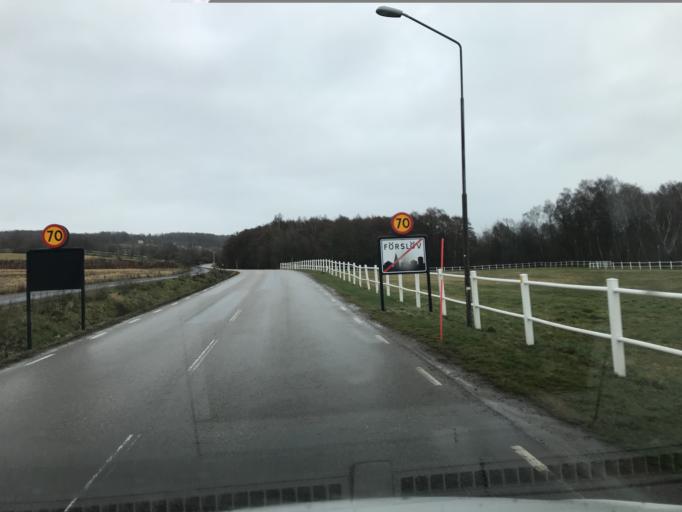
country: SE
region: Skane
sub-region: Bastads Kommun
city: Forslov
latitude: 56.3527
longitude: 12.8330
